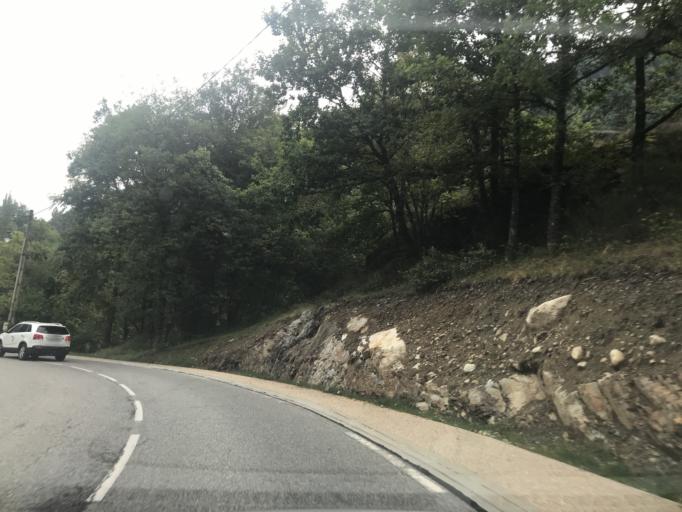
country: FR
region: Midi-Pyrenees
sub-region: Departement de la Haute-Garonne
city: Bagneres-de-Luchon
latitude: 42.7725
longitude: 0.6058
